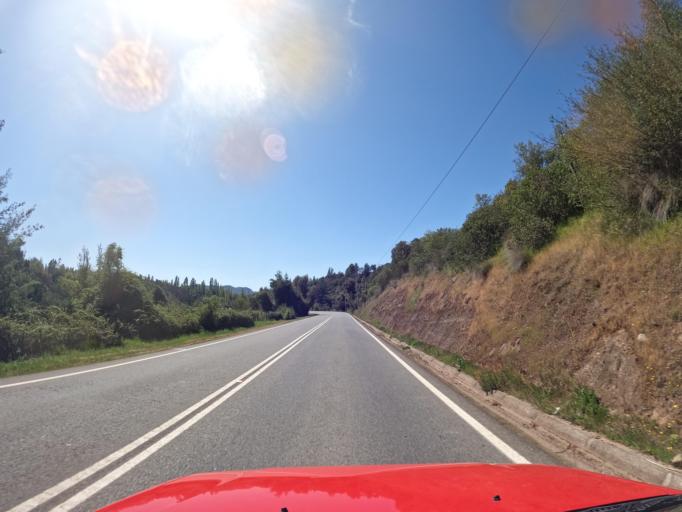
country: CL
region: Maule
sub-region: Provincia de Talca
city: San Clemente
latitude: -35.4640
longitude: -71.2698
